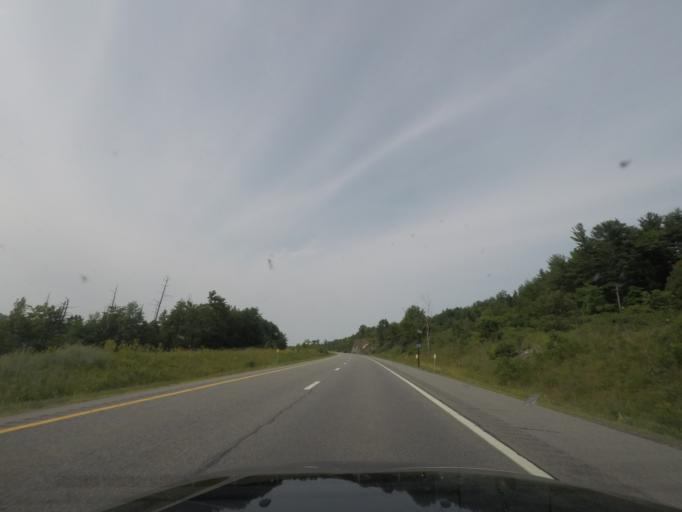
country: US
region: New York
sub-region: Essex County
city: Keeseville
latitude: 44.4272
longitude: -73.4917
